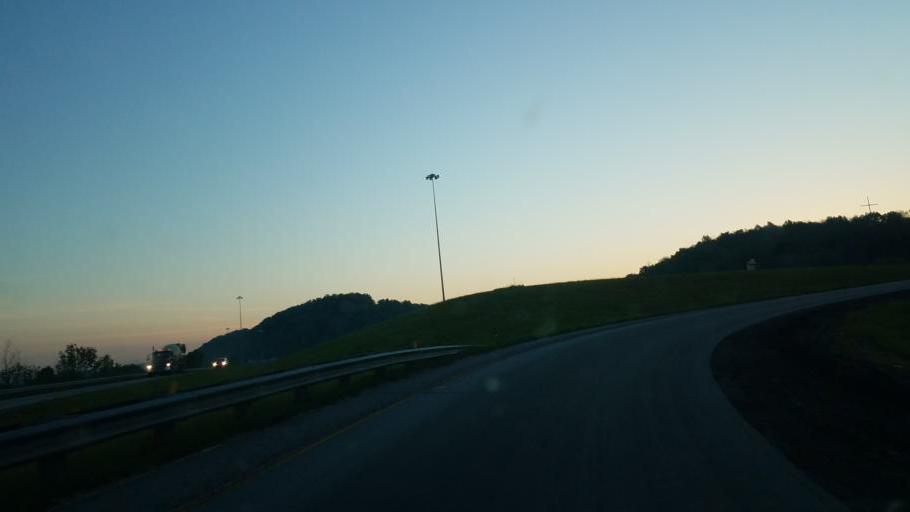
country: US
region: Ohio
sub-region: Guernsey County
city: Byesville
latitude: 39.9994
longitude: -81.5630
